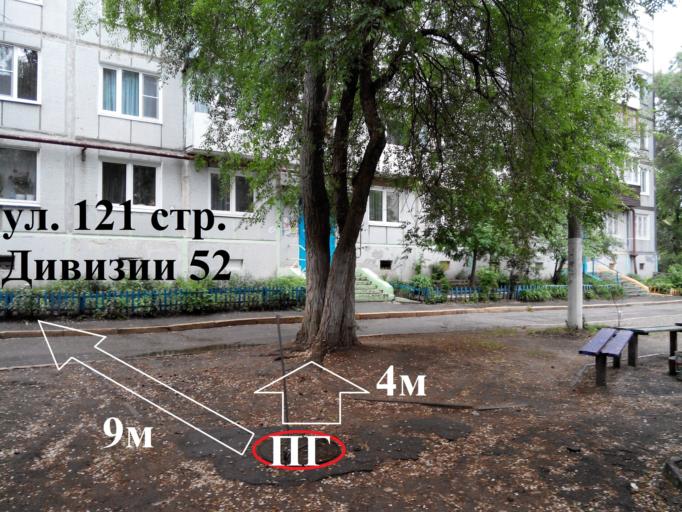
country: RU
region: Voronezj
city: Voronezh
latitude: 51.6460
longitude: 39.1638
